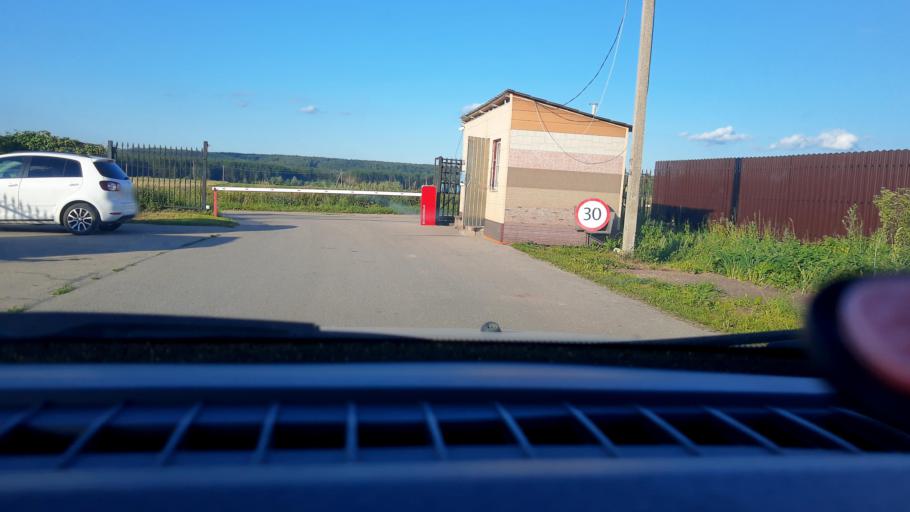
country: RU
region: Nizjnij Novgorod
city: Burevestnik
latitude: 56.0400
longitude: 43.8849
